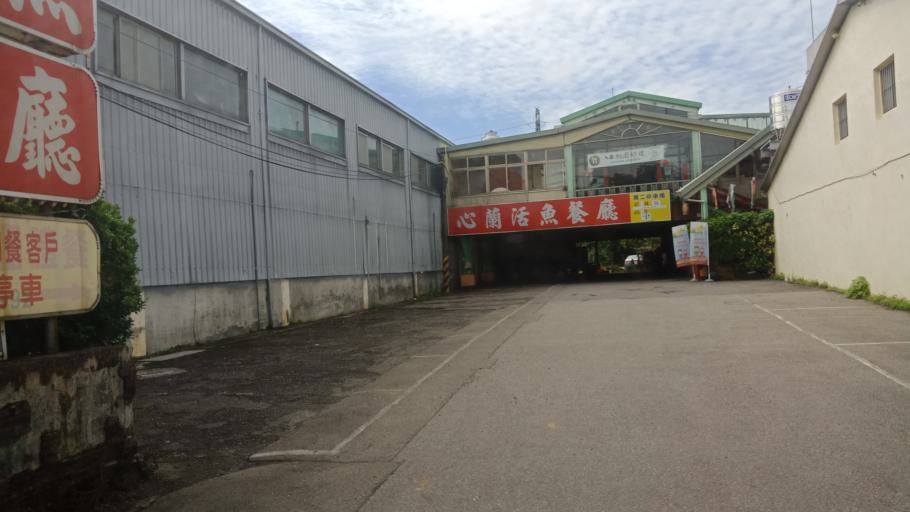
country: TW
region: Taiwan
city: Daxi
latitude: 24.8429
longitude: 121.2404
